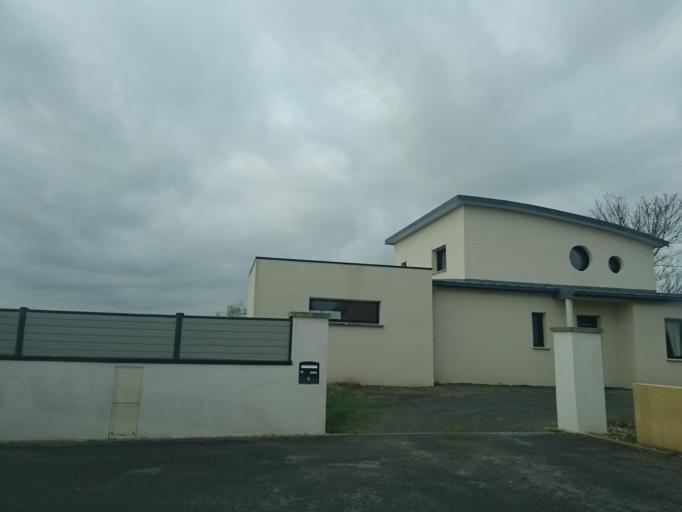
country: FR
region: Brittany
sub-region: Departement du Finistere
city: Le Drennec
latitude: 48.5414
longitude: -4.3683
